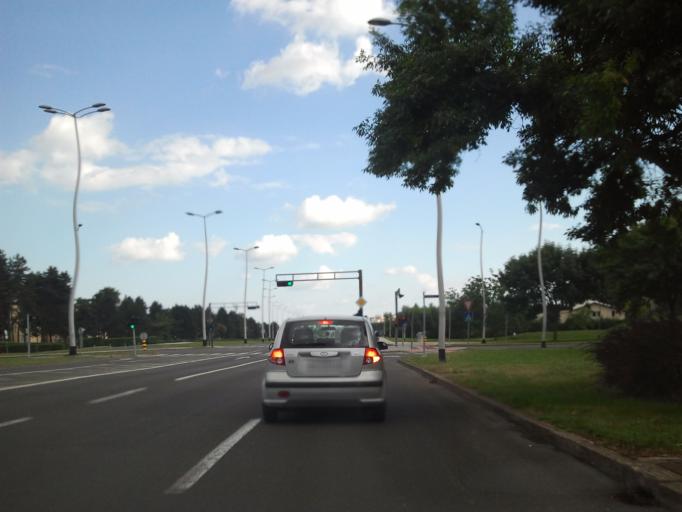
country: HR
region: Grad Zagreb
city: Novi Zagreb
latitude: 45.7739
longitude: 16.0034
